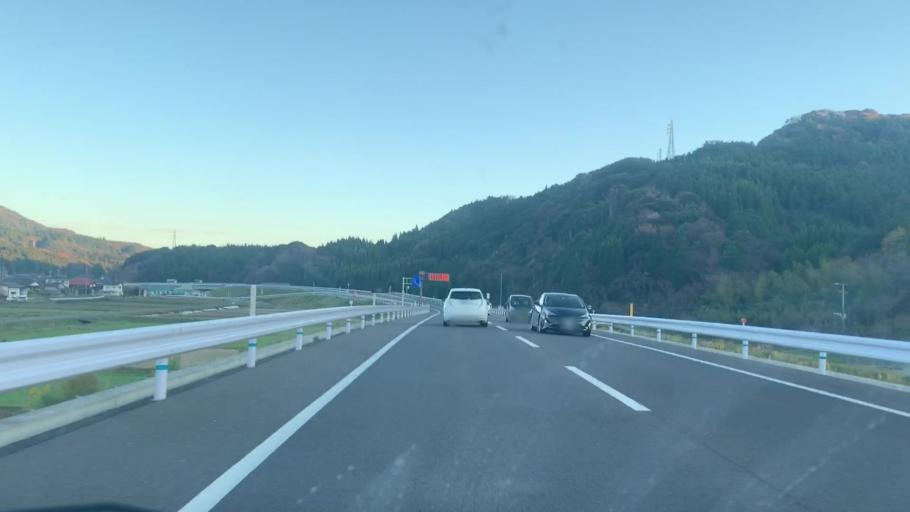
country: JP
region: Saga Prefecture
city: Takeocho-takeo
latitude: 33.2523
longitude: 129.9902
